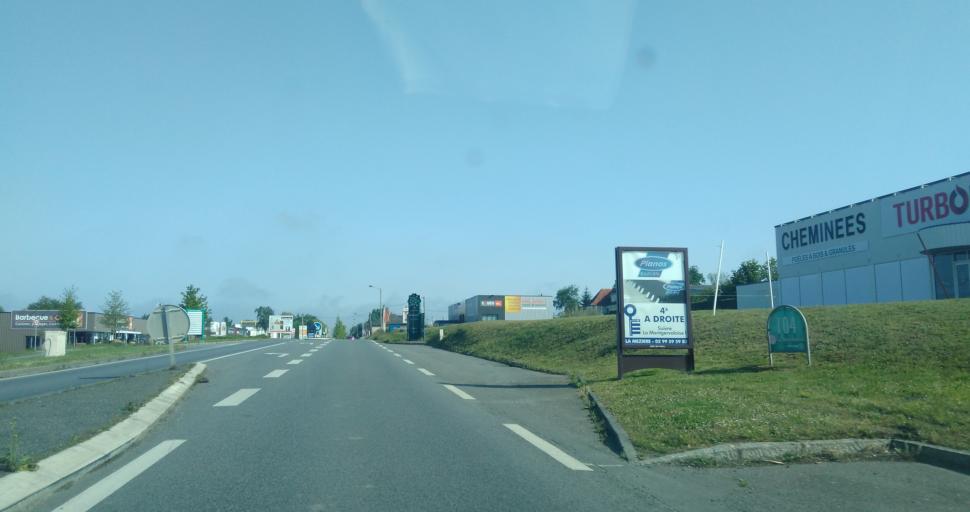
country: FR
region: Brittany
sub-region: Departement d'Ille-et-Vilaine
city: La Chapelle-des-Fougeretz
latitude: 48.1909
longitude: -1.7286
